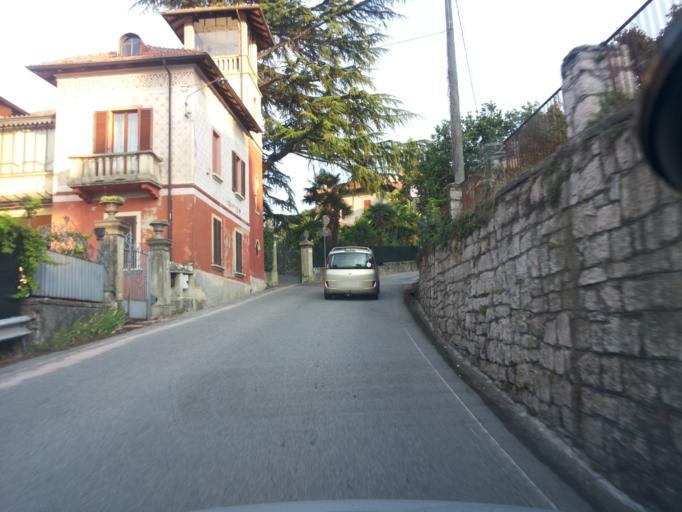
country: IT
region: Piedmont
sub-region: Provincia Verbano-Cusio-Ossola
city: Stresa
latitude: 45.8762
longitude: 8.5460
